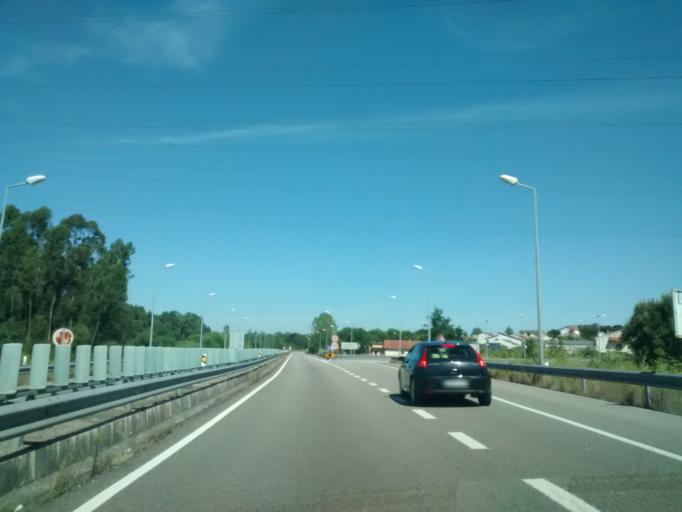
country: PT
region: Aveiro
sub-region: Anadia
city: Sangalhos
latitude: 40.4666
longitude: -8.4643
